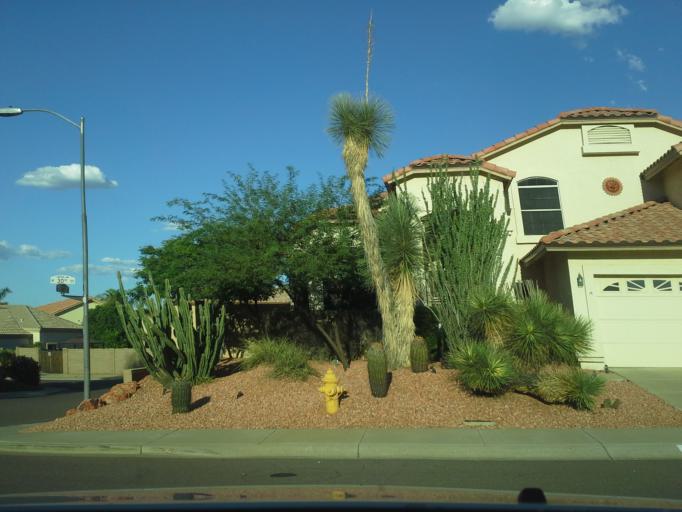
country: US
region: Arizona
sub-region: Maricopa County
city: Paradise Valley
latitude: 33.6139
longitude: -112.0181
